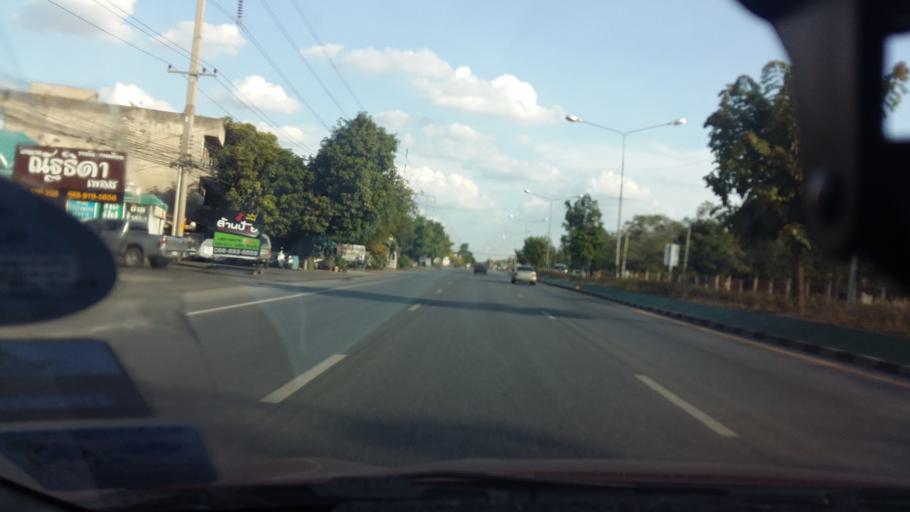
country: TH
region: Lop Buri
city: Lop Buri
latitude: 14.8435
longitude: 100.6435
